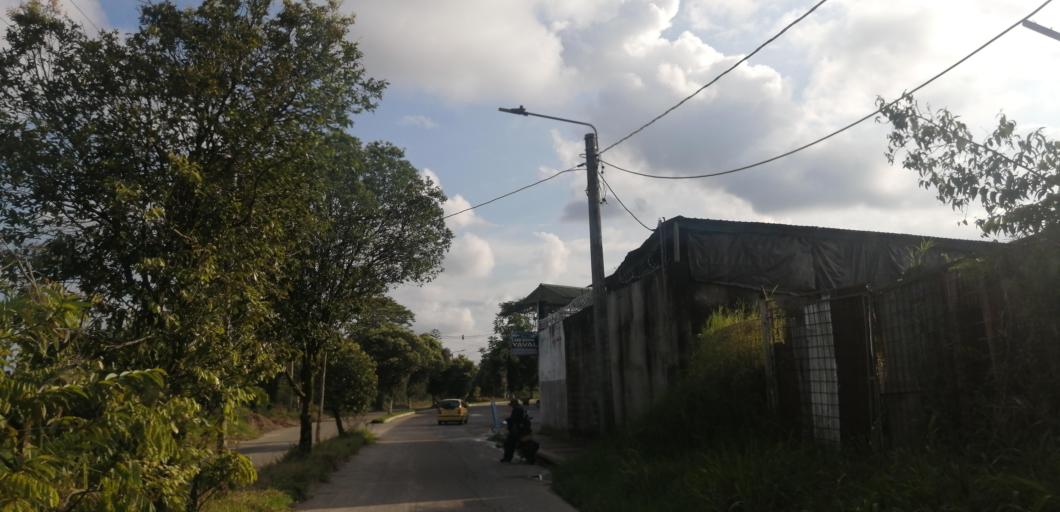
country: CO
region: Meta
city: Acacias
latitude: 3.9789
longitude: -73.7659
